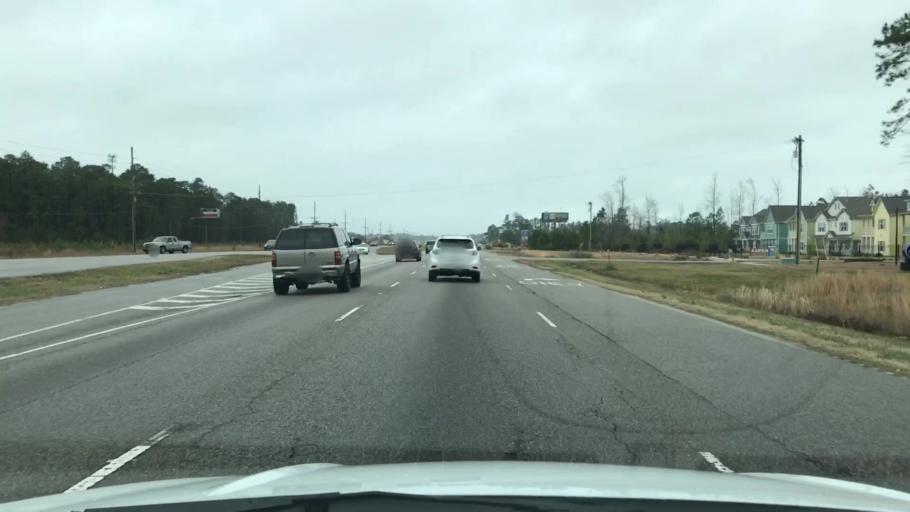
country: US
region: South Carolina
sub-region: Horry County
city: Red Hill
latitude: 33.7831
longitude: -78.9899
